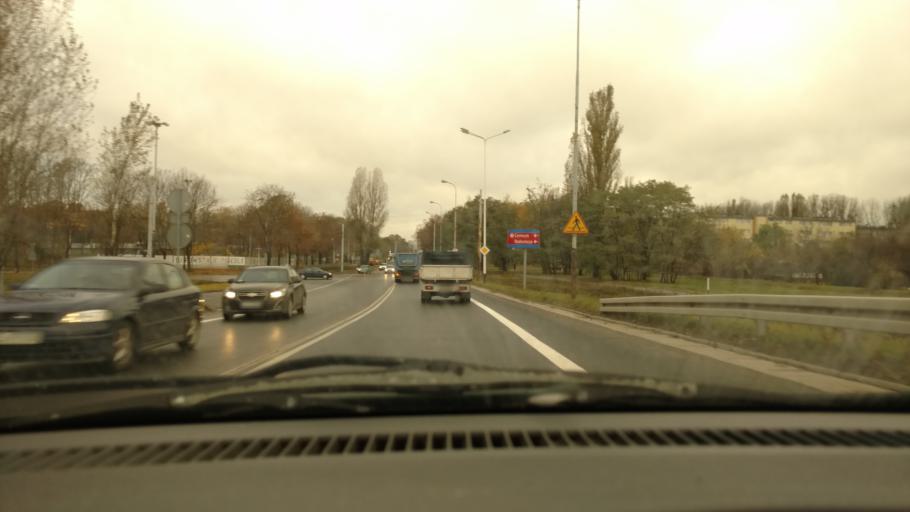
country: PL
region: Lodz Voivodeship
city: Lodz
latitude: 51.7773
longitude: 19.5002
